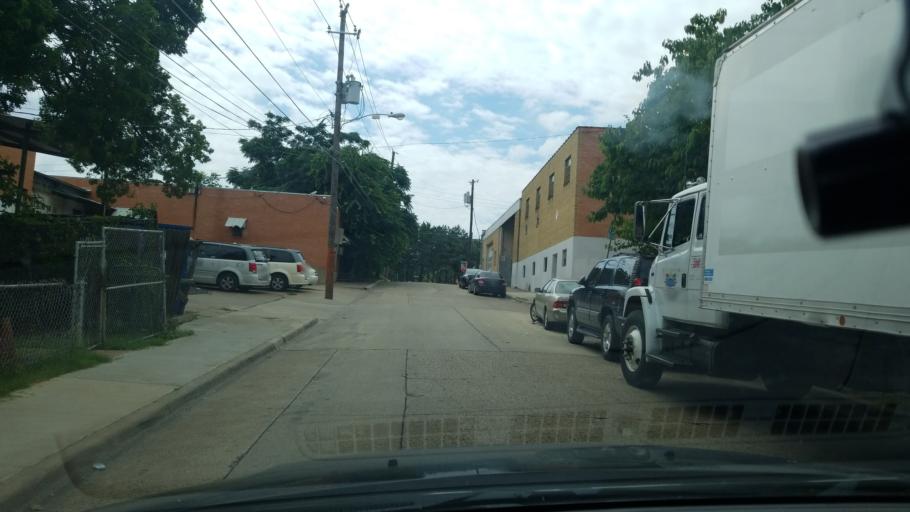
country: US
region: Texas
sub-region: Dallas County
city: Dallas
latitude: 32.7702
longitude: -96.7947
